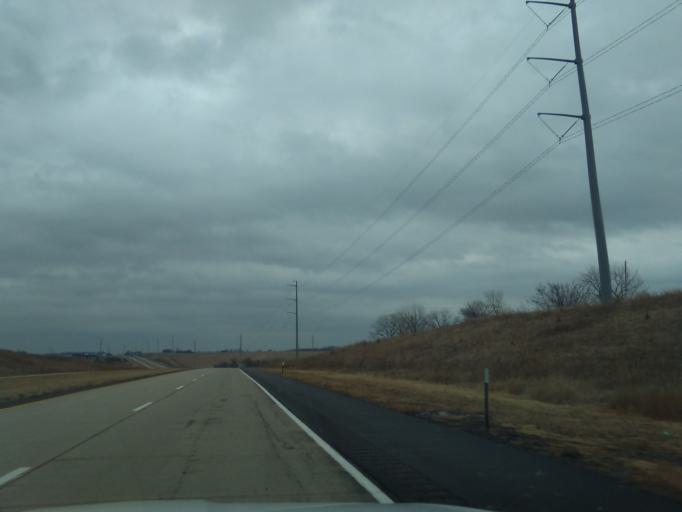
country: US
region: Nebraska
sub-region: Otoe County
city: Syracuse
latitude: 40.6689
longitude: -96.1578
